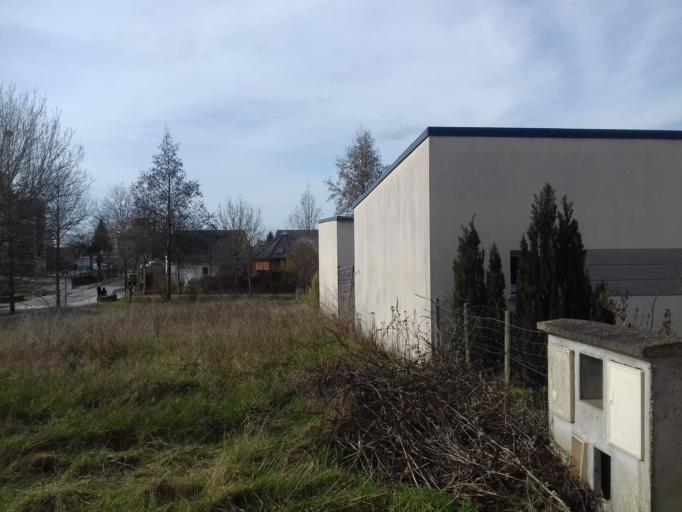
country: FR
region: Picardie
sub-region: Departement de la Somme
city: Amiens
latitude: 49.8786
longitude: 2.2784
